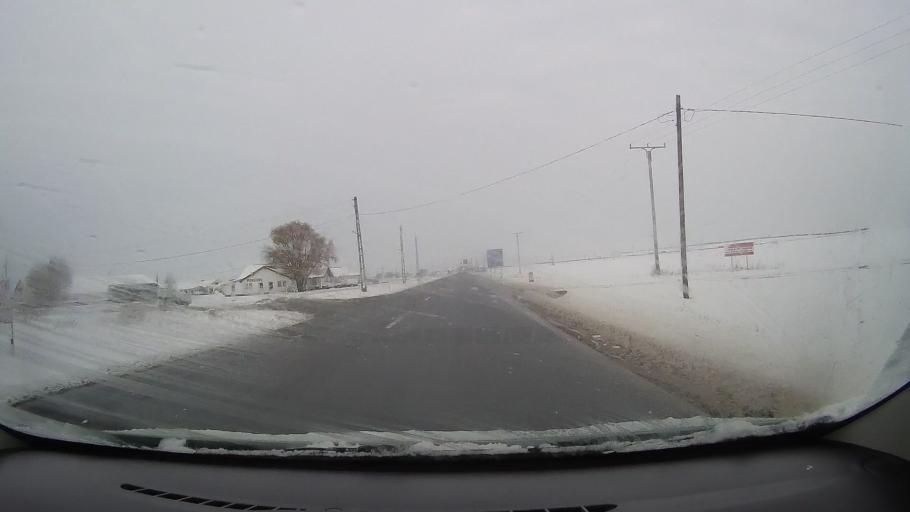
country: RO
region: Alba
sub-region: Municipiul Sebes
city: Lancram
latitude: 45.9697
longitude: 23.5275
